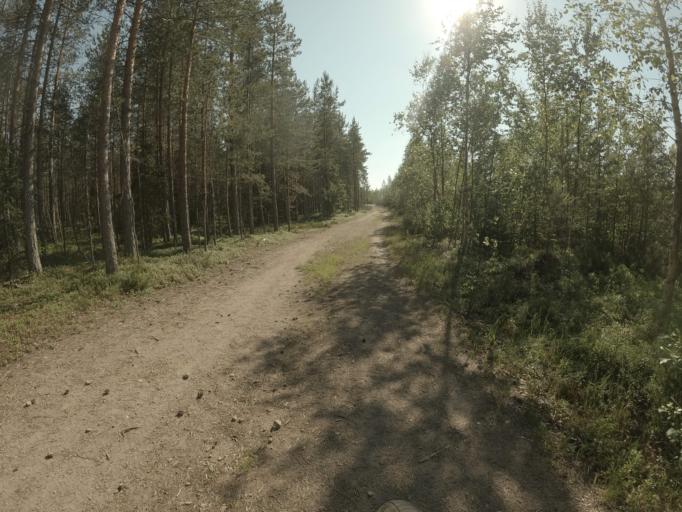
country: RU
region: Leningrad
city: Yakovlevo
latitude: 60.4584
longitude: 29.2745
